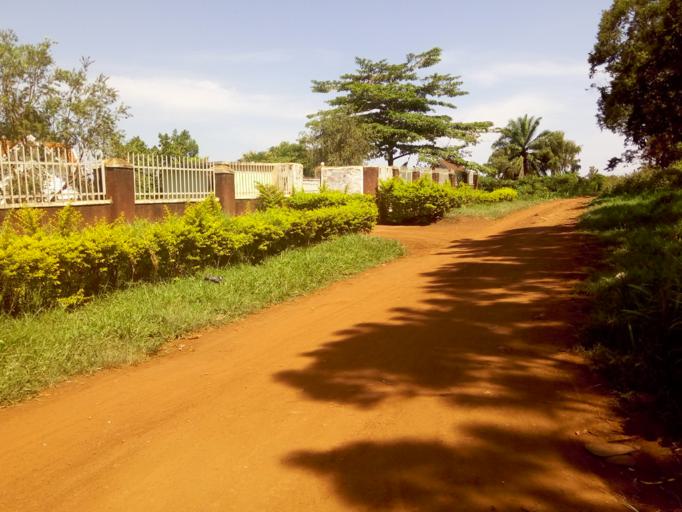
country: UG
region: Western Region
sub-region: Masindi District
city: Masindi
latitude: 1.6890
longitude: 31.7142
